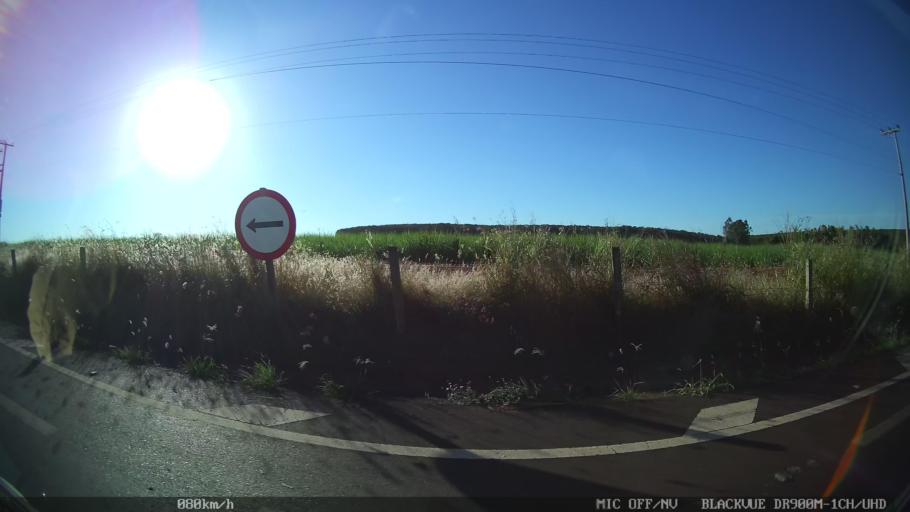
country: BR
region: Sao Paulo
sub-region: Guapiacu
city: Guapiacu
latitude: -20.7633
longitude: -49.1872
